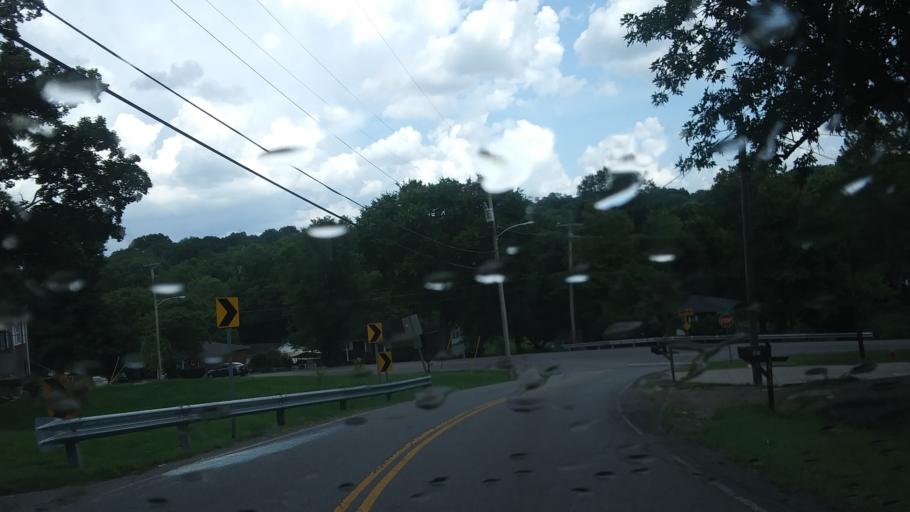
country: US
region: Tennessee
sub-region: Davidson County
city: Oak Hill
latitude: 36.0632
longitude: -86.7050
